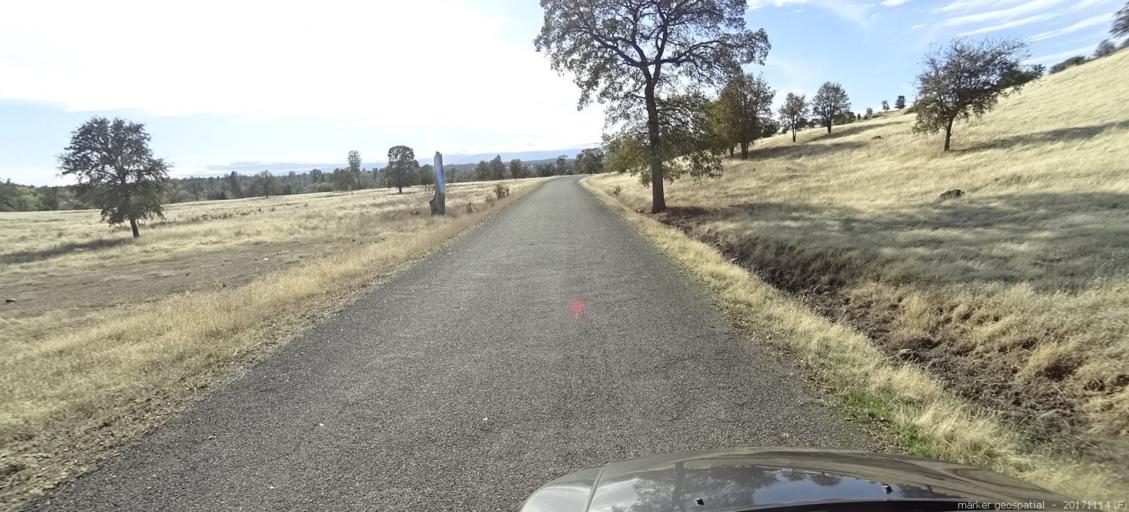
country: US
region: California
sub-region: Shasta County
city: Shasta
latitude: 40.3829
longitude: -122.5472
